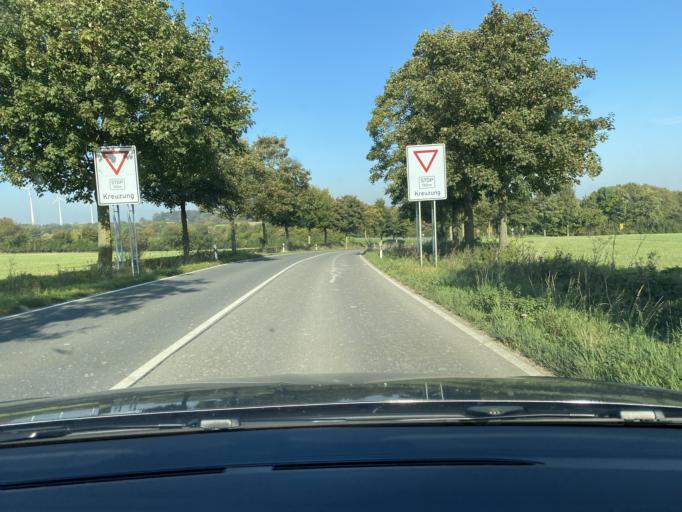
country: DE
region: North Rhine-Westphalia
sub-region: Regierungsbezirk Munster
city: Horstmar
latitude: 52.0763
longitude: 7.2936
